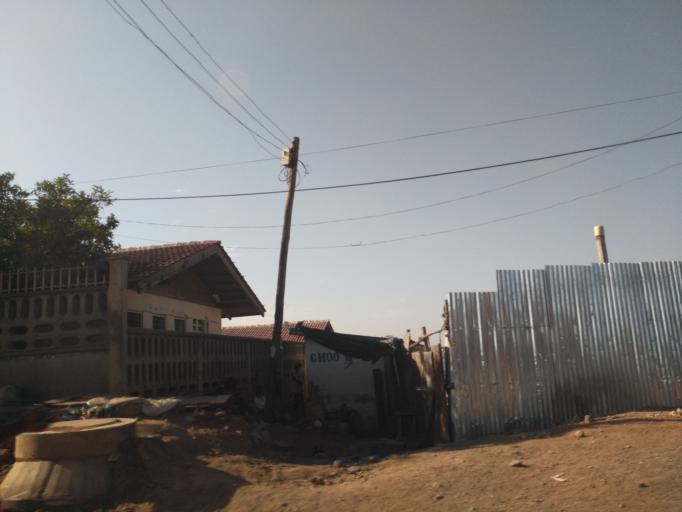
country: TZ
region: Mwanza
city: Mwanza
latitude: -2.5064
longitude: 32.8944
